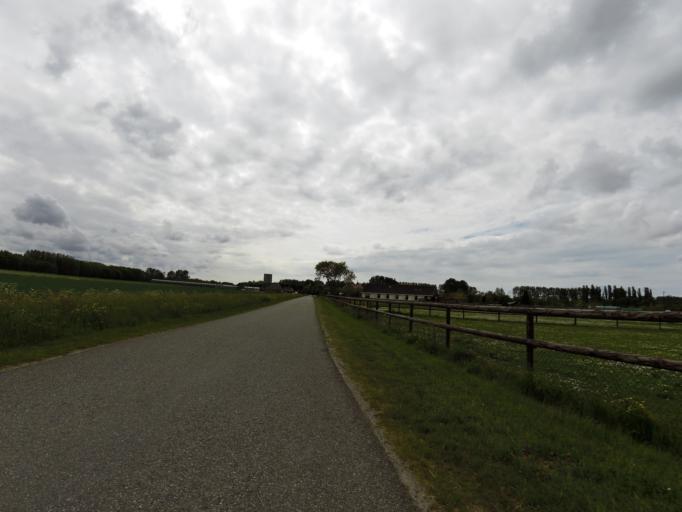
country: NL
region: South Holland
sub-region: Gemeente Hellevoetsluis
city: Nieuw-Helvoet
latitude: 51.8626
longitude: 4.0895
